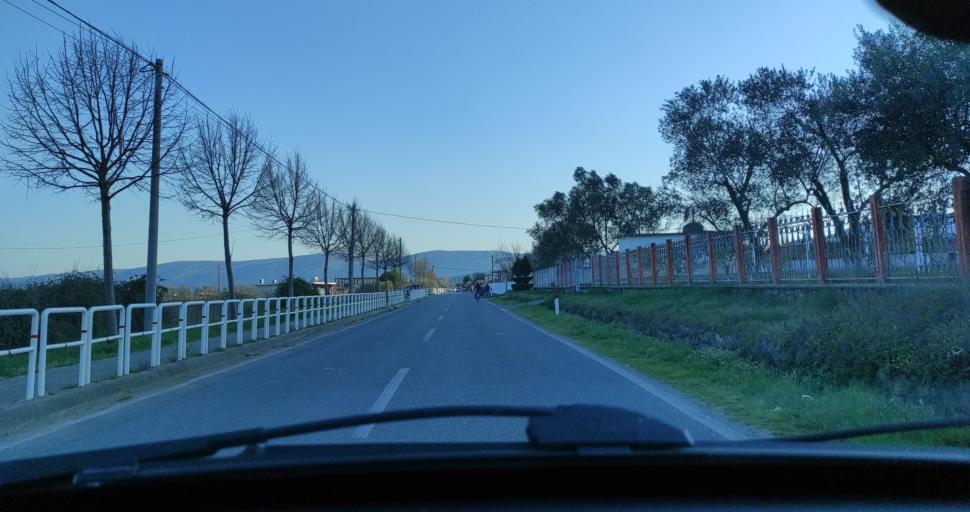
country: AL
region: Shkoder
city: Vukatane
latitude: 41.9658
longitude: 19.5383
